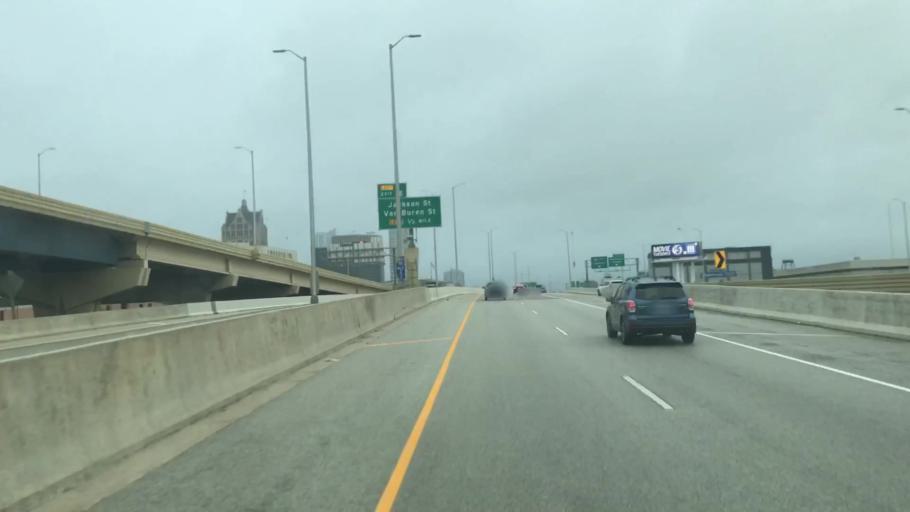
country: US
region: Wisconsin
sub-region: Milwaukee County
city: Milwaukee
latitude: 43.0355
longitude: -87.9219
